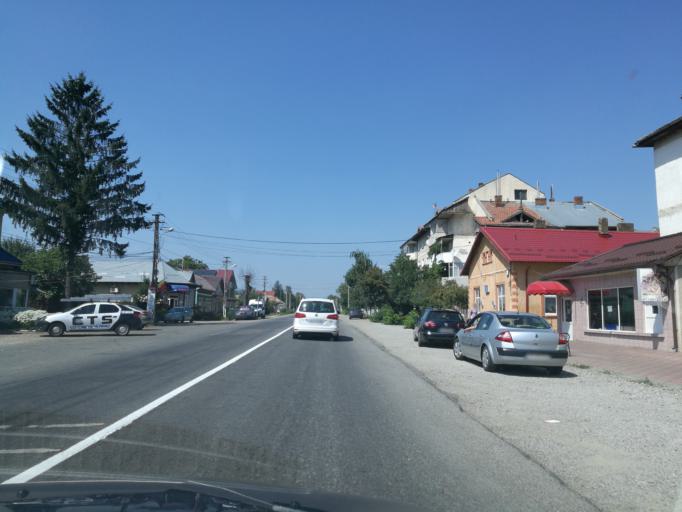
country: RO
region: Neamt
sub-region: Comuna Roznov
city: Roznov
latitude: 46.8386
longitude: 26.5062
